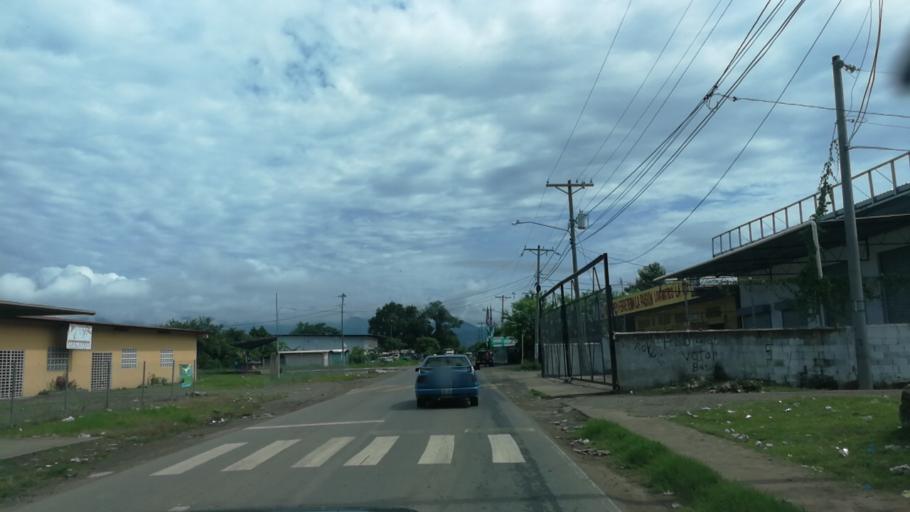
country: PA
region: Panama
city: Paso Blanco
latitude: 9.1270
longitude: -79.2529
